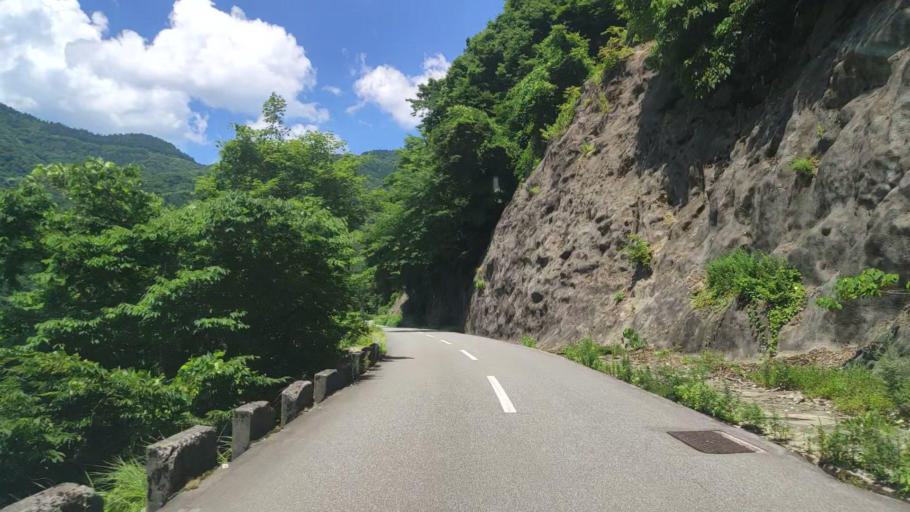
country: JP
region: Fukui
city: Ono
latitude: 35.8969
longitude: 136.5195
